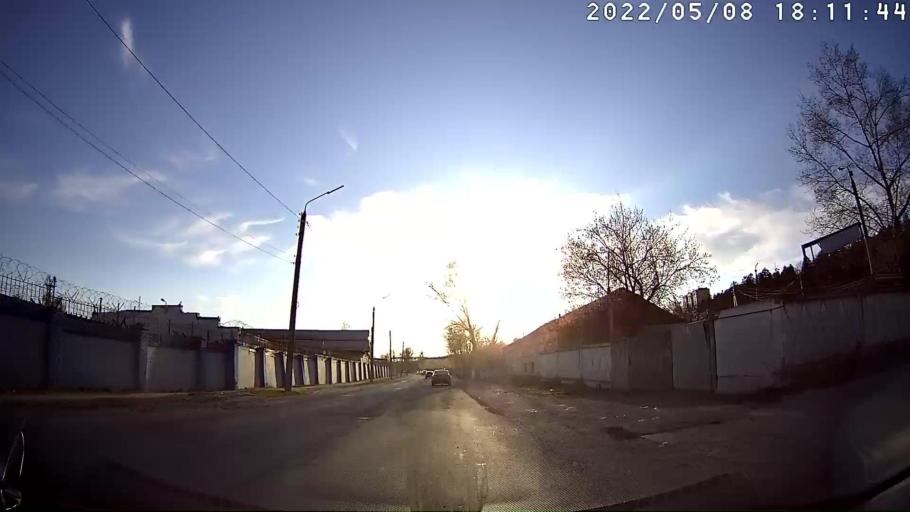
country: RU
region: Tatarstan
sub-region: Zelenodol'skiy Rayon
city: Zelenodolsk
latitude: 55.8406
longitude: 48.5081
